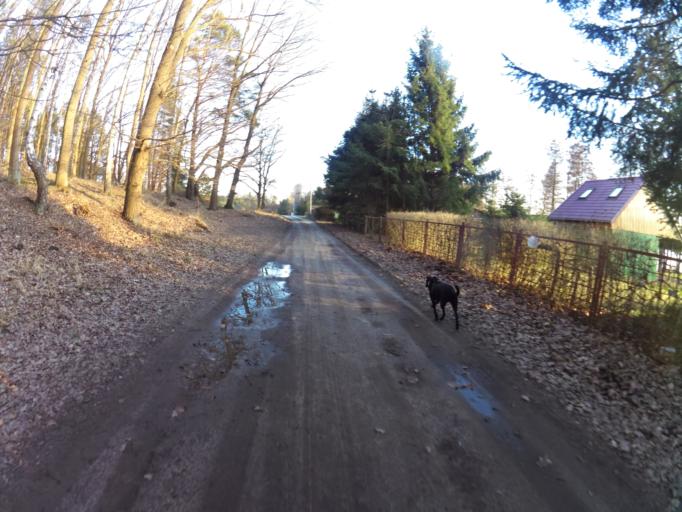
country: PL
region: West Pomeranian Voivodeship
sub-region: Powiat mysliborski
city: Debno
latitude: 52.8252
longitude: 14.7797
